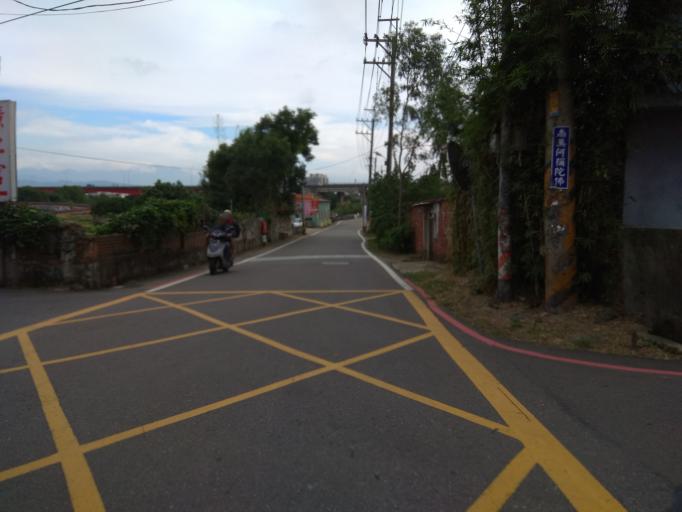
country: TW
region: Taiwan
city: Daxi
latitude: 24.9304
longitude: 121.2051
